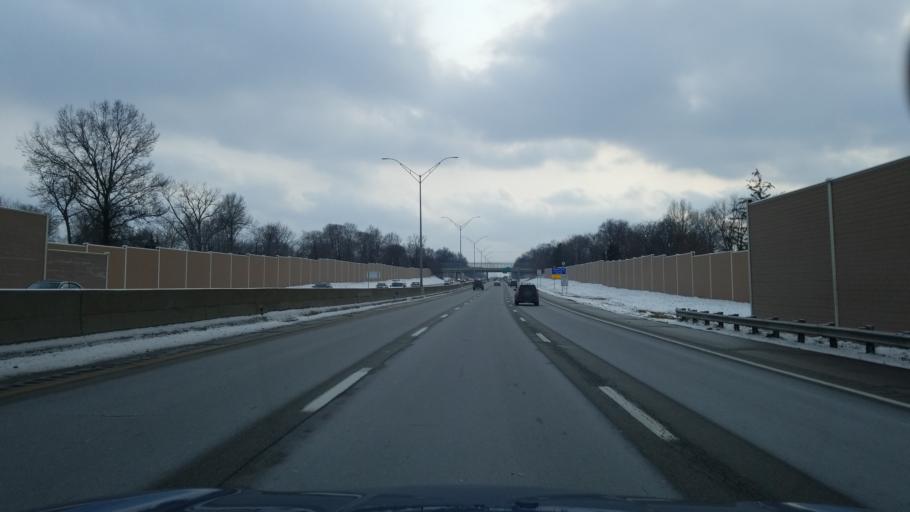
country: US
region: Ohio
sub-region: Cuyahoga County
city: Brook Park
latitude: 41.3926
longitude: -81.8158
